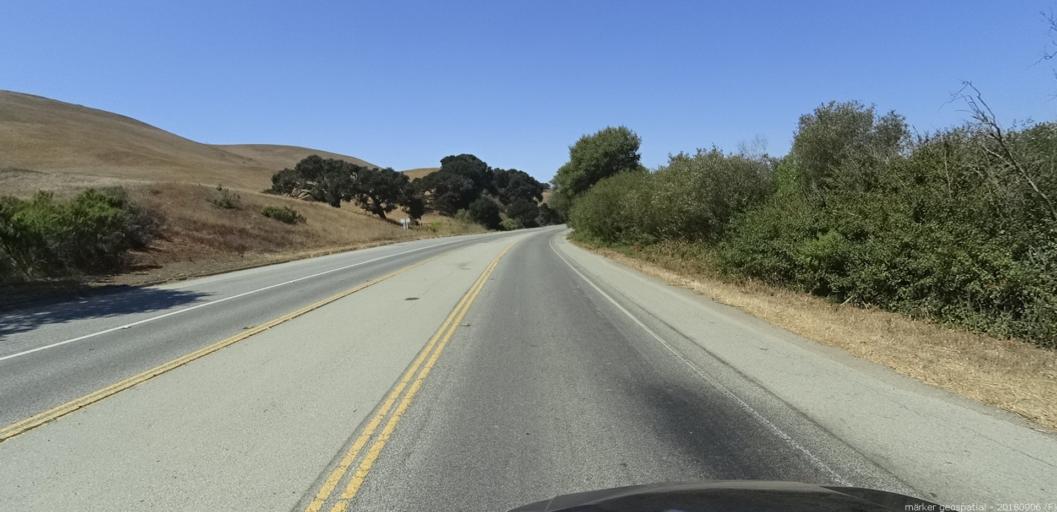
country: US
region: California
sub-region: Monterey County
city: Salinas
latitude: 36.6094
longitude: -121.6499
